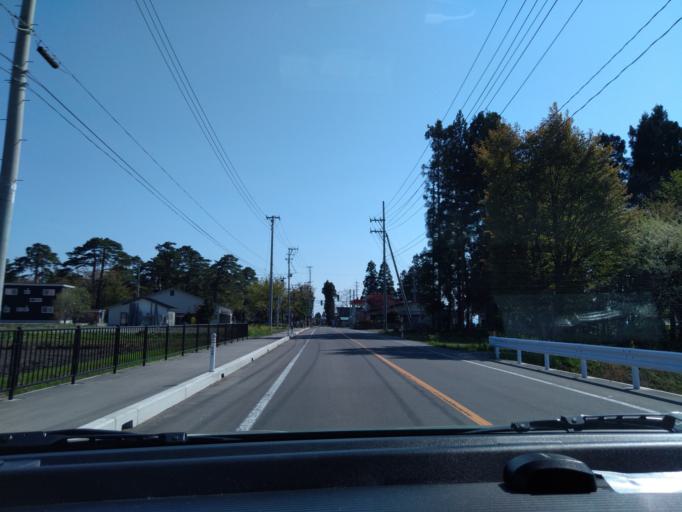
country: JP
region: Akita
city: Omagari
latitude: 39.4741
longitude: 140.5857
